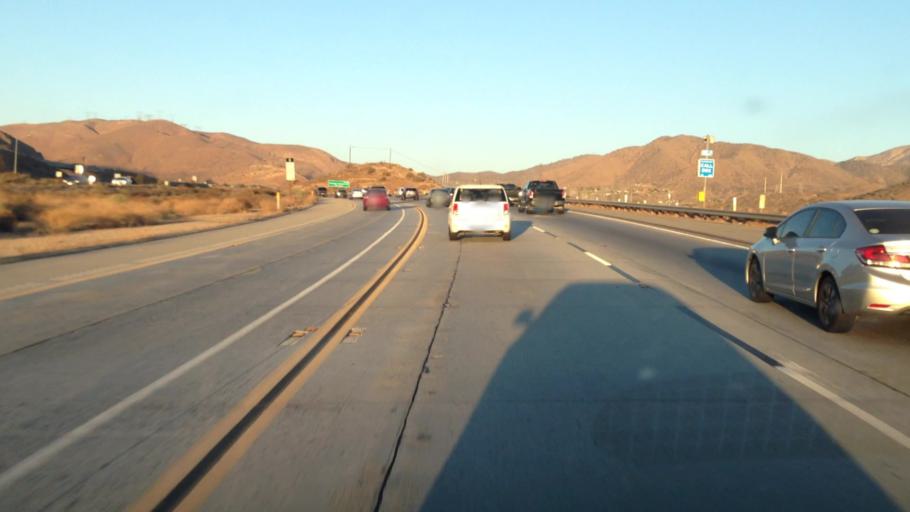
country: US
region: California
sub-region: Los Angeles County
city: Vincent
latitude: 34.4851
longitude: -118.1447
